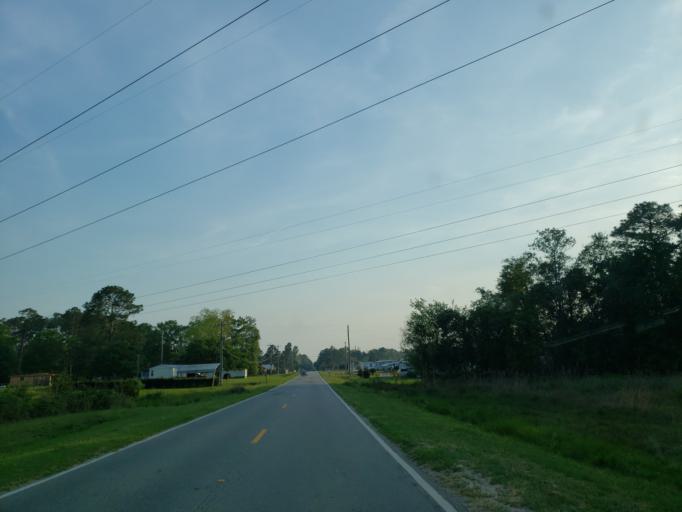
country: US
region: Georgia
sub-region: Cook County
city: Sparks
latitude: 31.1787
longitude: -83.4295
